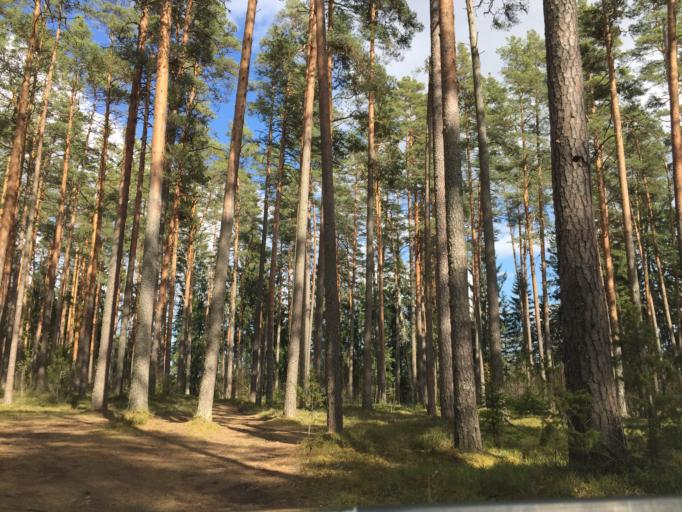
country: LV
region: Gulbenes Rajons
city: Gulbene
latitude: 57.2680
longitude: 26.5516
